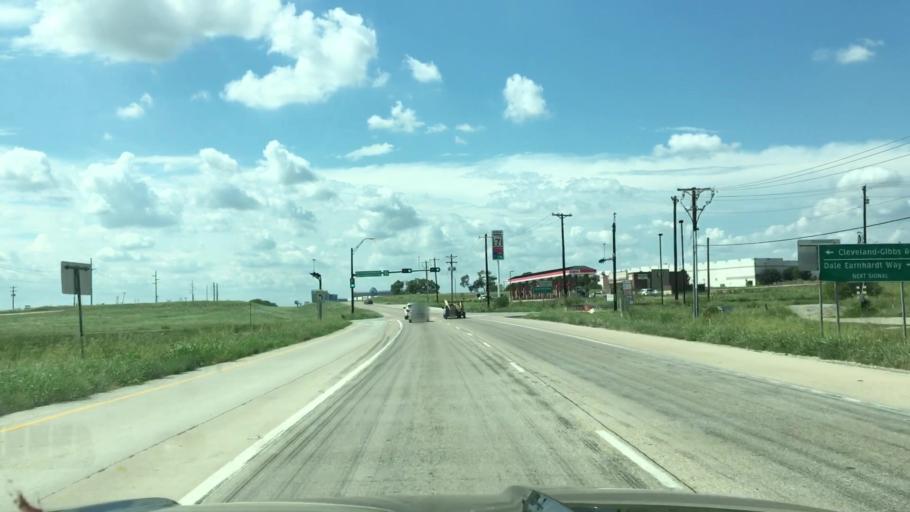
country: US
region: Texas
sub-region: Denton County
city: Roanoke
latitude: 33.0237
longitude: -97.2557
